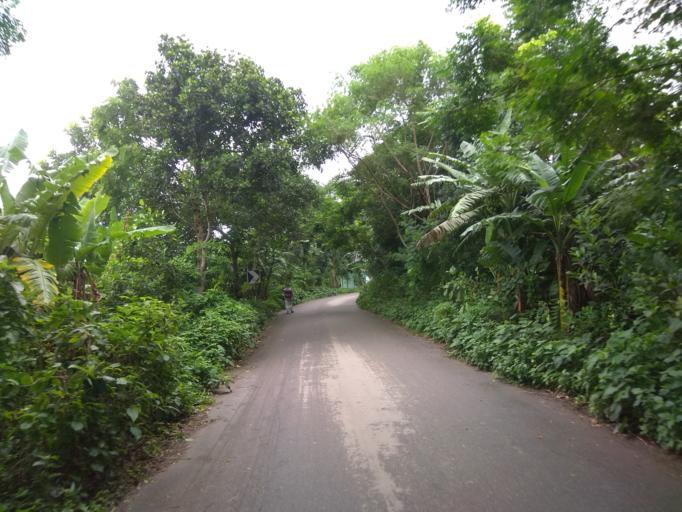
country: BD
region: Dhaka
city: Dohar
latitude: 23.4227
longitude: 90.0643
